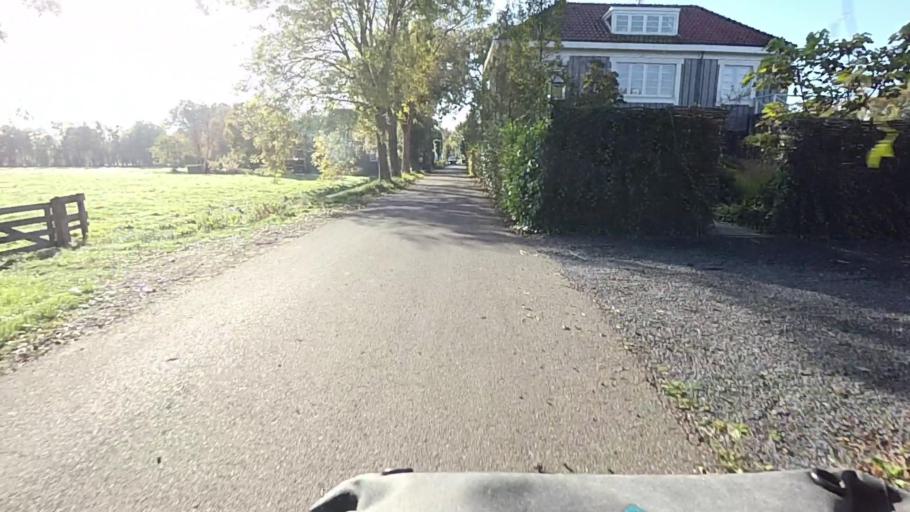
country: NL
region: Utrecht
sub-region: Stichtse Vecht
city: Vreeland
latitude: 52.2262
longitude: 5.0340
